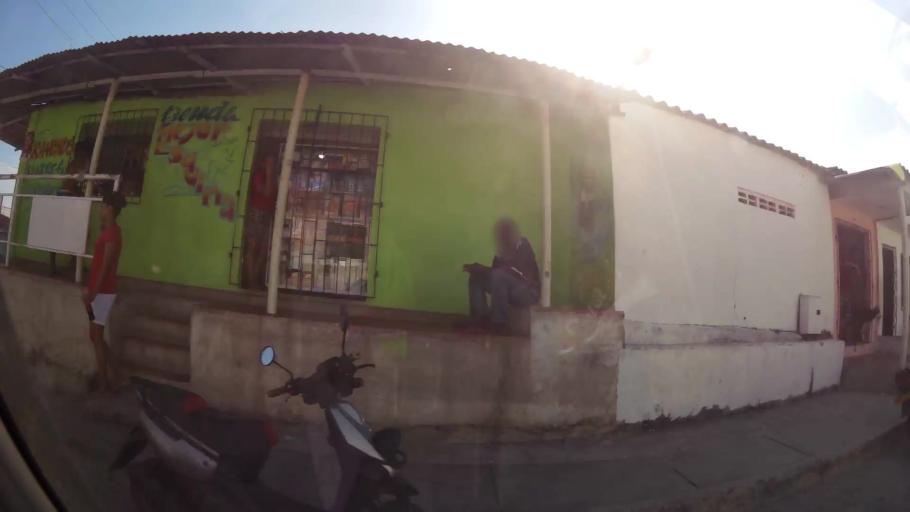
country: CO
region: Atlantico
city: Barranquilla
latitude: 10.9315
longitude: -74.8225
